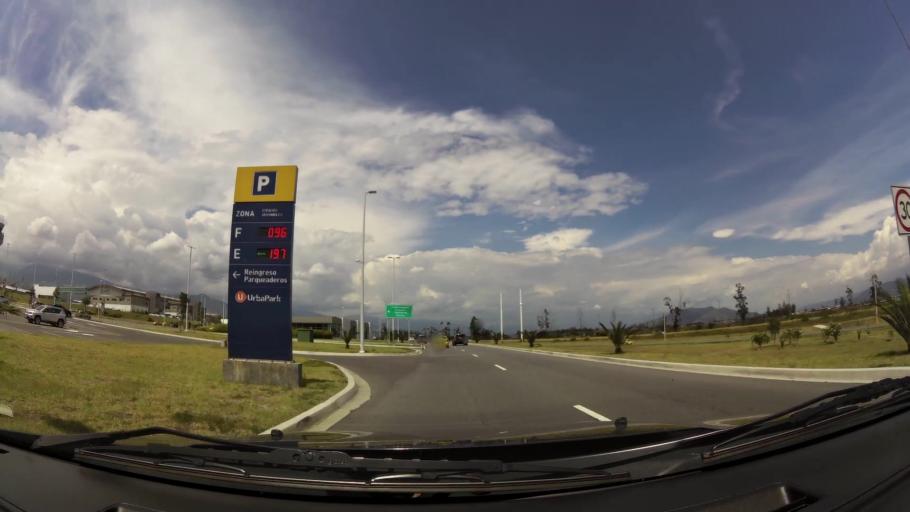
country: EC
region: Pichincha
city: Quito
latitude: -0.1264
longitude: -78.3623
